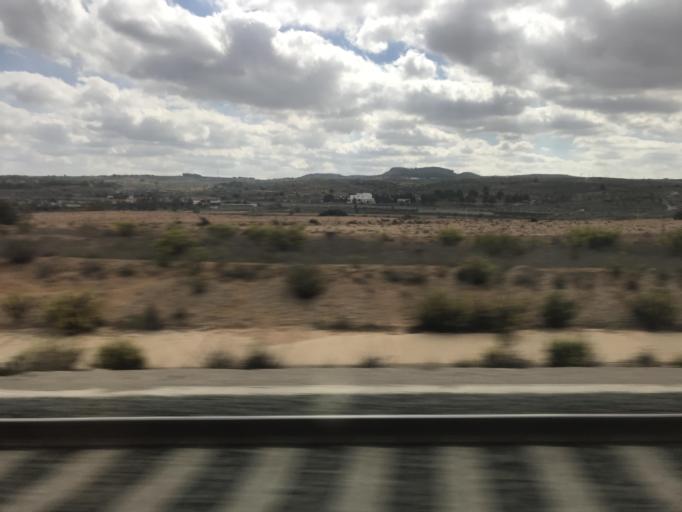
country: ES
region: Castille-La Mancha
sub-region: Provincia de Albacete
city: Almansa
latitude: 38.8830
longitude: -1.1481
